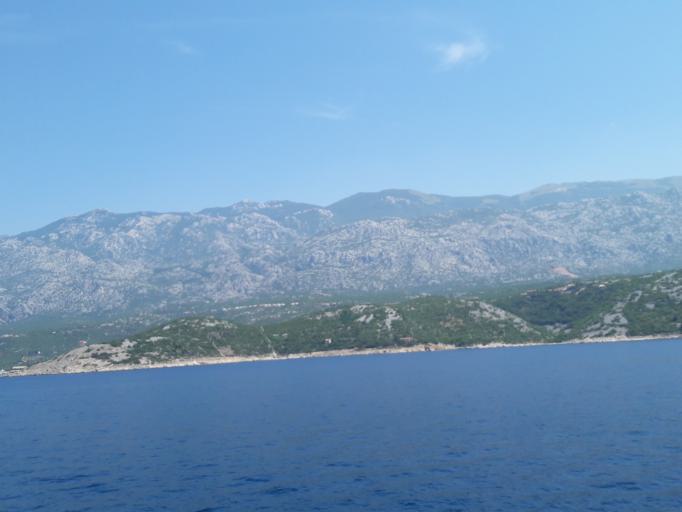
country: HR
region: Primorsko-Goranska
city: Banjol
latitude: 44.7104
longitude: 14.8791
